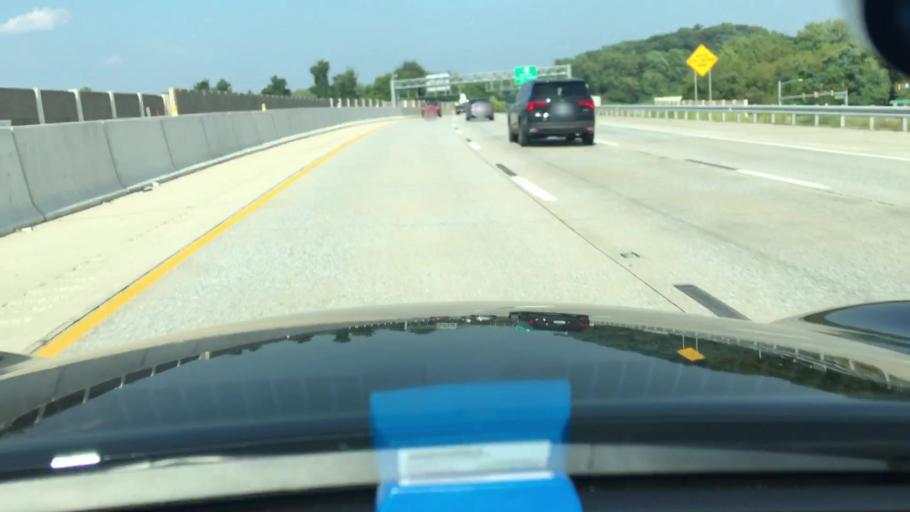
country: US
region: Pennsylvania
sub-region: Chester County
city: Malvern
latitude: 40.0507
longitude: -75.5637
